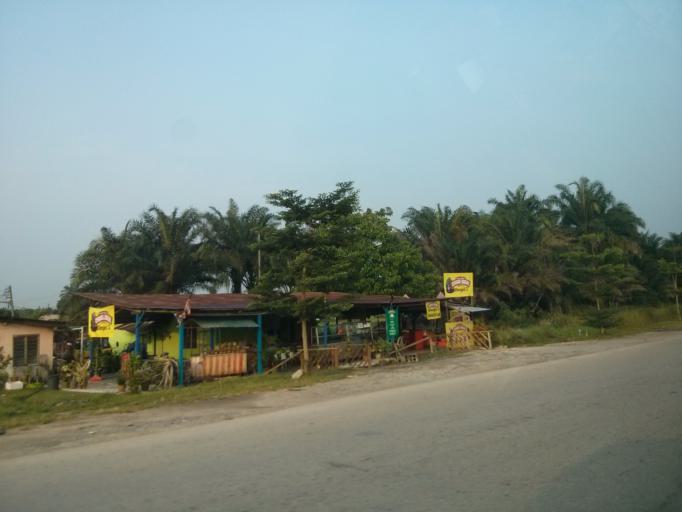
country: MY
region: Putrajaya
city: Putrajaya
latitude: 2.8596
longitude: 101.6926
